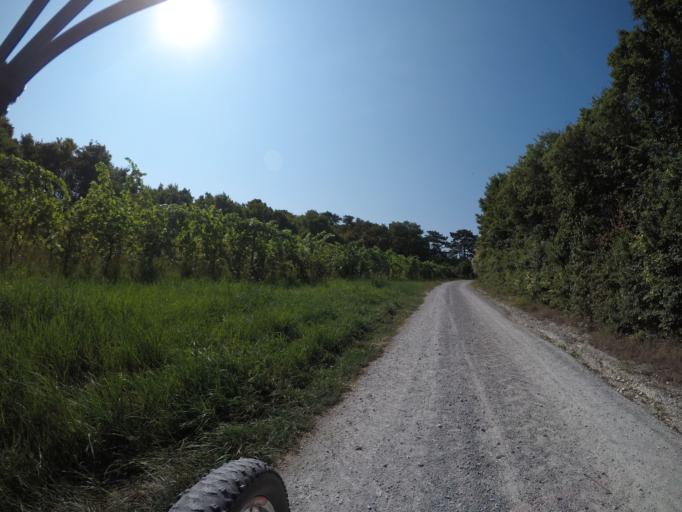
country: AT
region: Lower Austria
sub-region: Politischer Bezirk Baden
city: Hirtenberg
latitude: 47.9476
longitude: 16.1697
